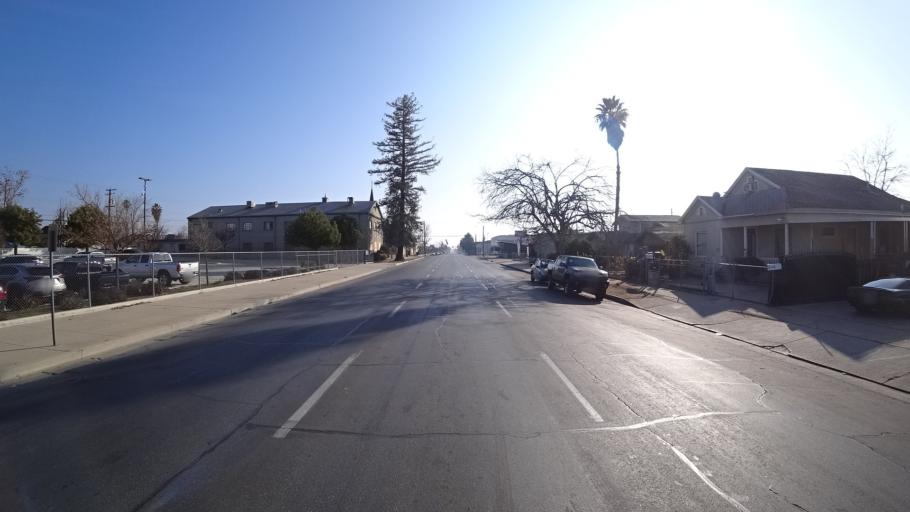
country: US
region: California
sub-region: Kern County
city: Bakersfield
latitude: 35.3819
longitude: -118.9907
